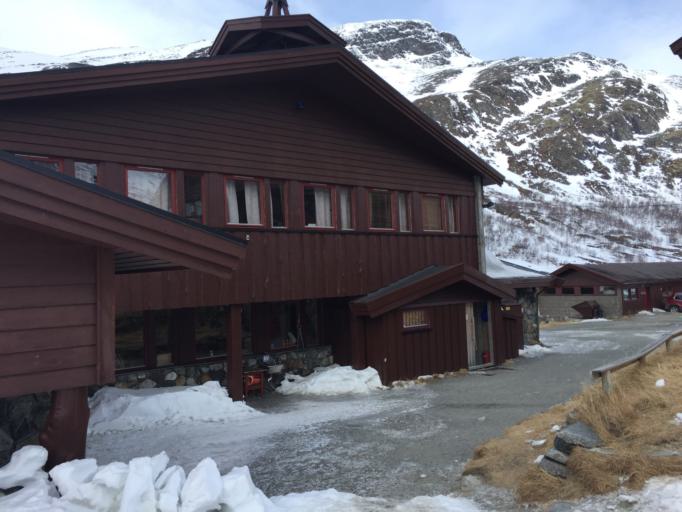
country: NO
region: Oppland
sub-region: Lom
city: Fossbergom
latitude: 61.6249
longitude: 8.4048
